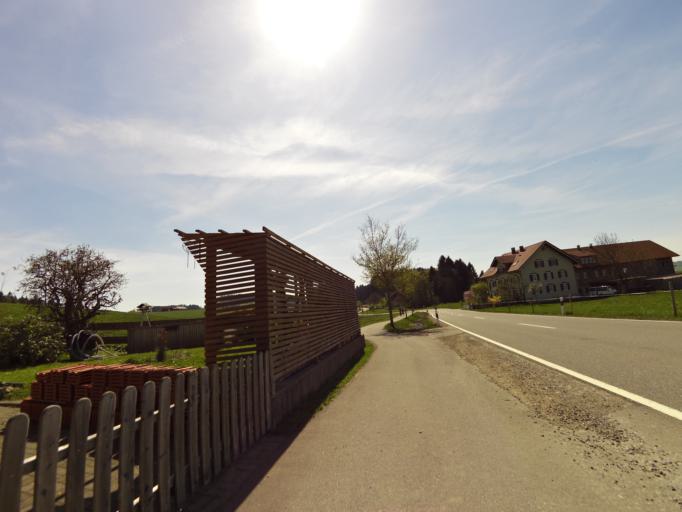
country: DE
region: Bavaria
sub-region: Swabia
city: Rothenbach
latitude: 47.5964
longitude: 9.9545
